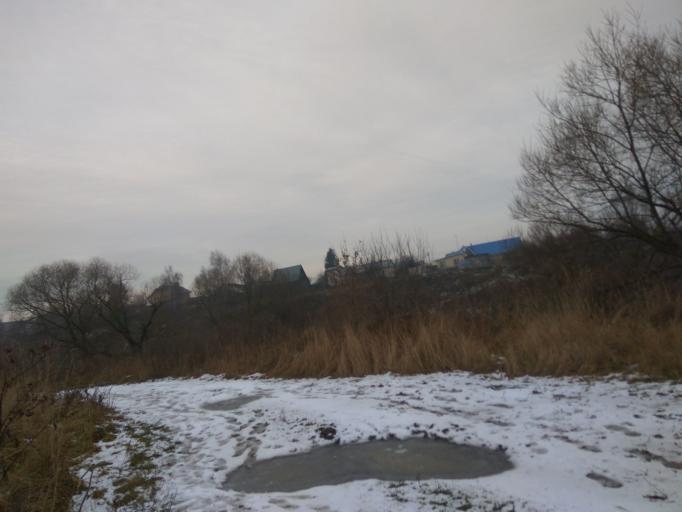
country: RU
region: Moskovskaya
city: Gorki-Leninskiye
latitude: 55.4774
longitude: 37.7984
